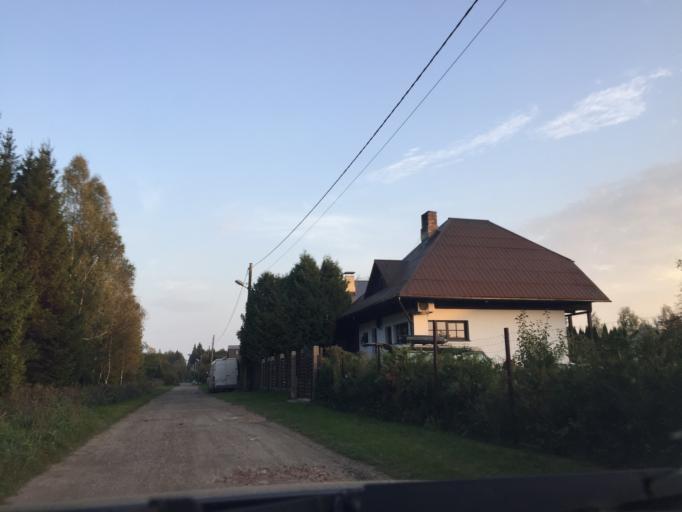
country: LV
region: Salaspils
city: Salaspils
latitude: 56.9200
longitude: 24.4290
